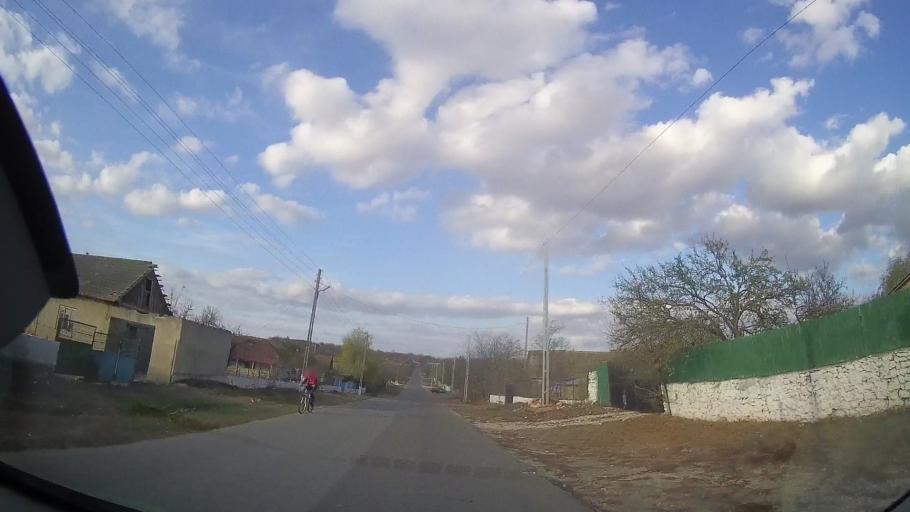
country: RO
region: Constanta
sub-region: Comuna Cerchezu
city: Cerchezu
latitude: 43.8551
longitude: 28.1012
